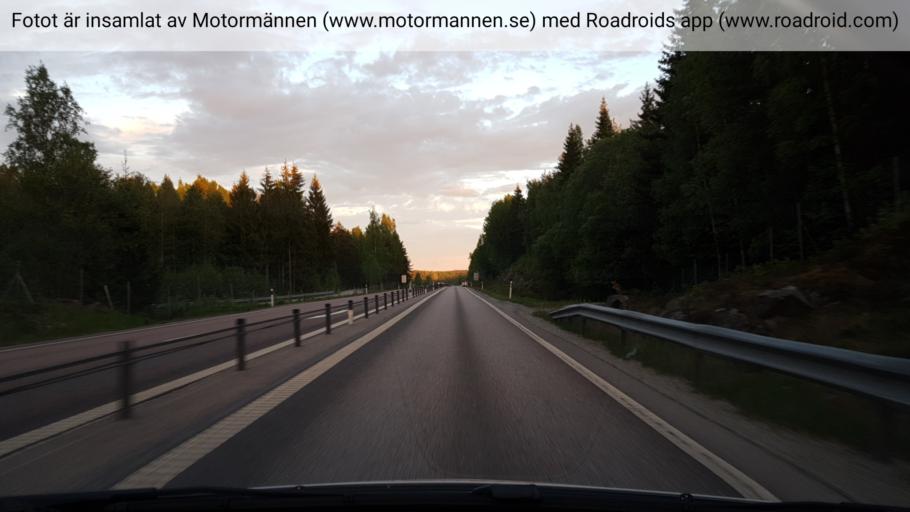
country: SE
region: Vaestmanland
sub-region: Norbergs Kommun
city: Norberg
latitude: 59.8995
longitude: 15.9798
